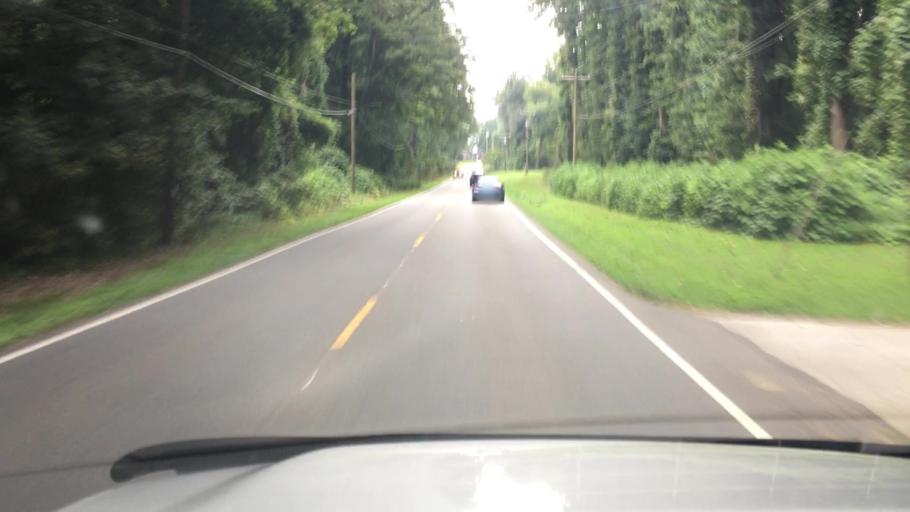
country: US
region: North Carolina
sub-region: Mecklenburg County
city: Huntersville
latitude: 35.3563
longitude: -80.8926
